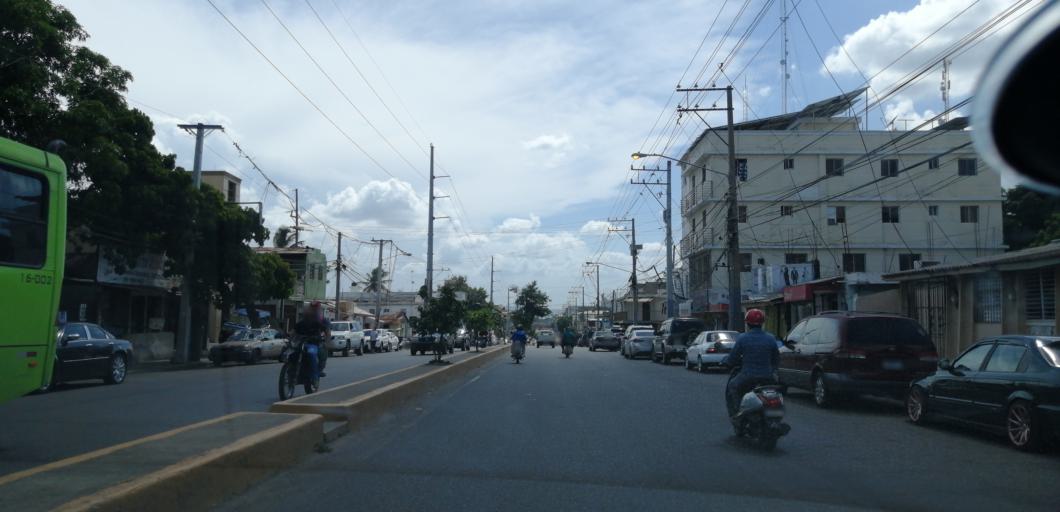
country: DO
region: Santiago
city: Santiago de los Caballeros
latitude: 19.4869
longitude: -70.7244
